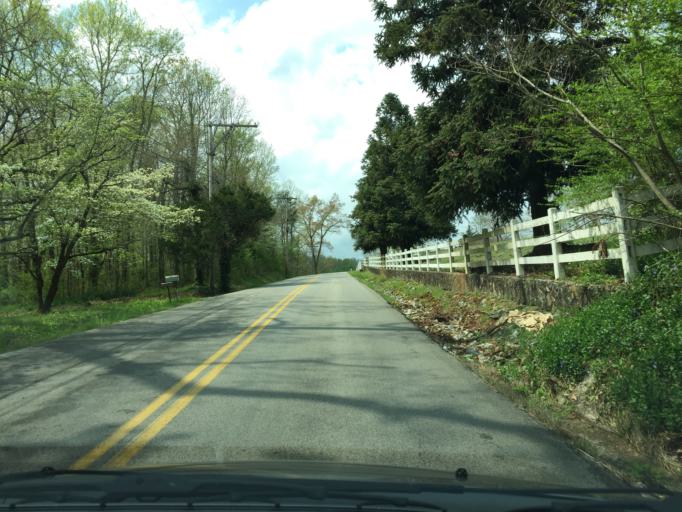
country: US
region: Tennessee
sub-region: Hamilton County
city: Red Bank
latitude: 35.1376
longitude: -85.2813
